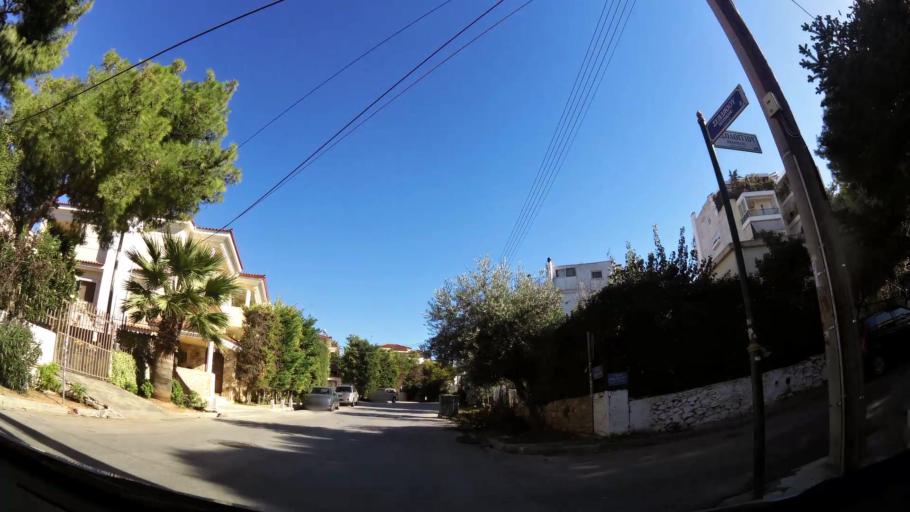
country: GR
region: Attica
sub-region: Nomarchia Athinas
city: Nea Erythraia
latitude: 38.0965
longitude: 23.8129
